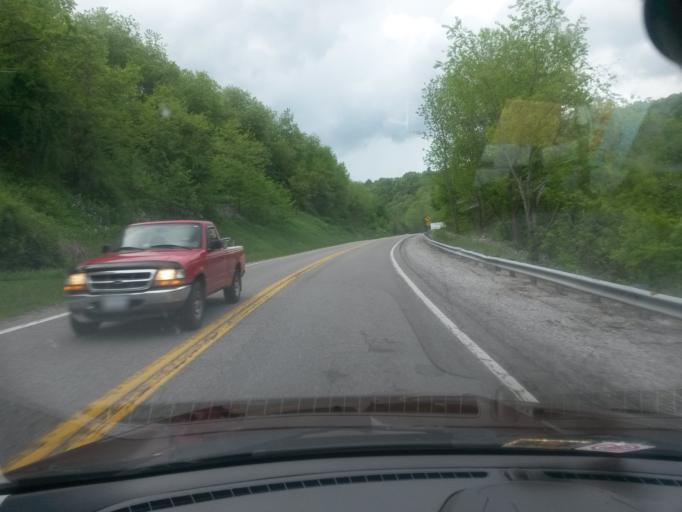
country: US
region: Virginia
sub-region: Floyd County
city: Floyd
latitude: 36.9331
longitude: -80.3352
